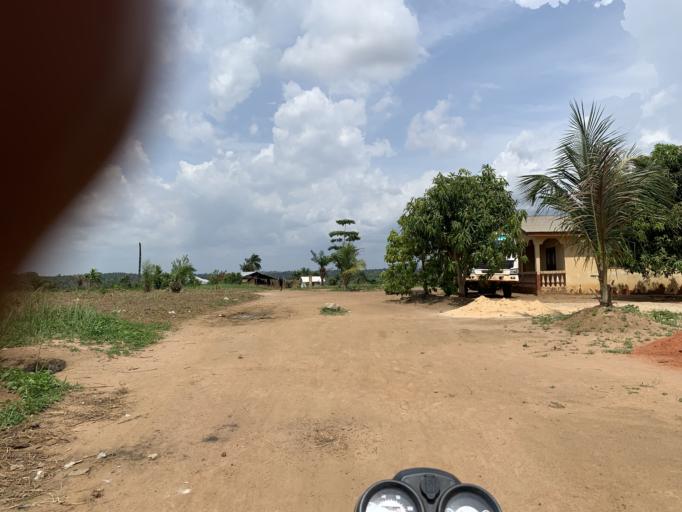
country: SL
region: Western Area
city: Waterloo
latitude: 8.3614
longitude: -13.0429
